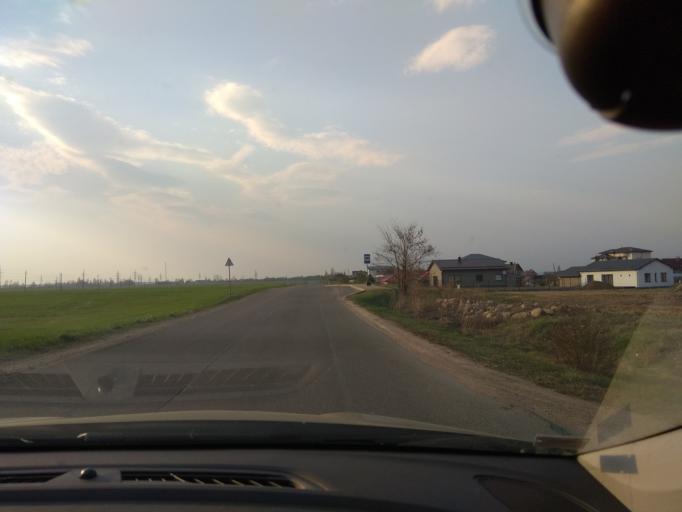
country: LT
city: Baltoji Voke
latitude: 54.6036
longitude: 25.1346
